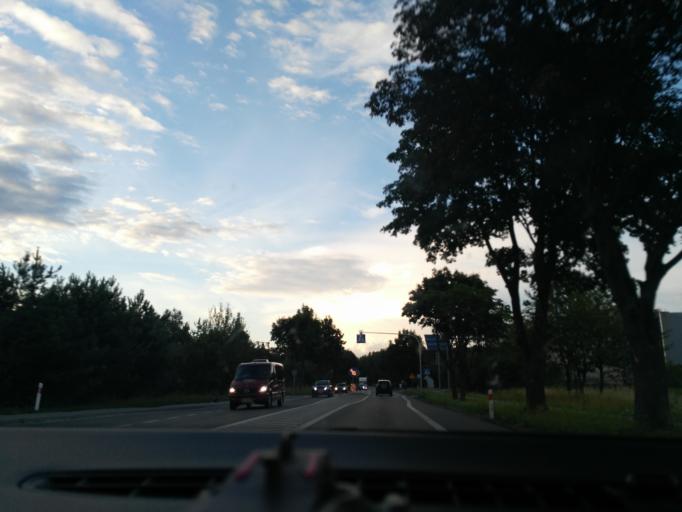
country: PL
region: Lublin Voivodeship
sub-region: Powiat lubelski
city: Niemce
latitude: 51.3728
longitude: 22.6334
